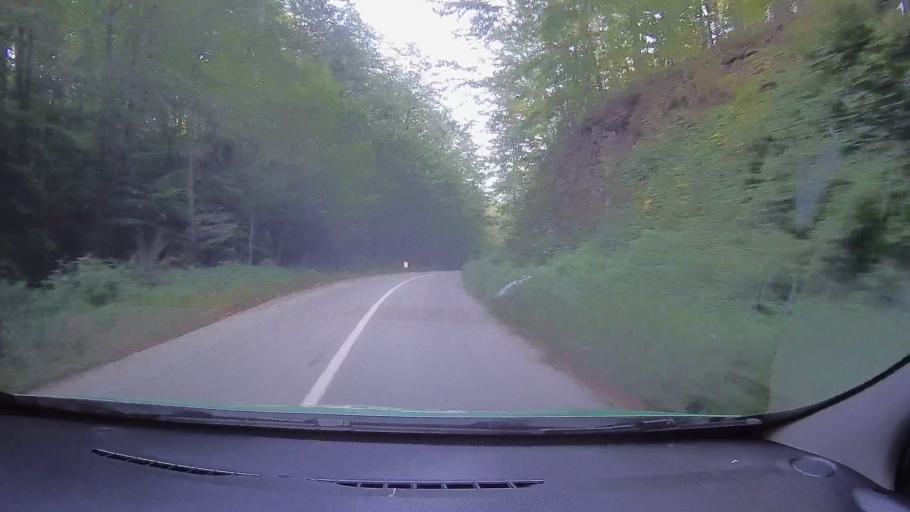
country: RO
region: Timis
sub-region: Comuna Nadrag
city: Nadrag
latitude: 45.6734
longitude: 22.1757
